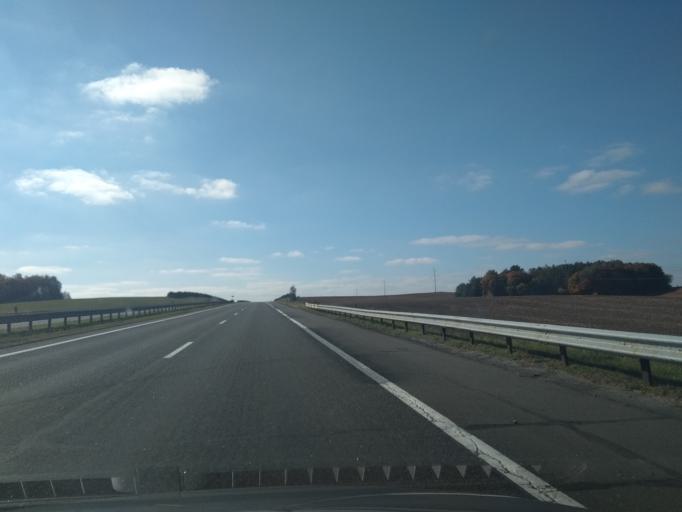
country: BY
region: Minsk
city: Haradzyeya
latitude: 53.3358
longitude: 26.4315
